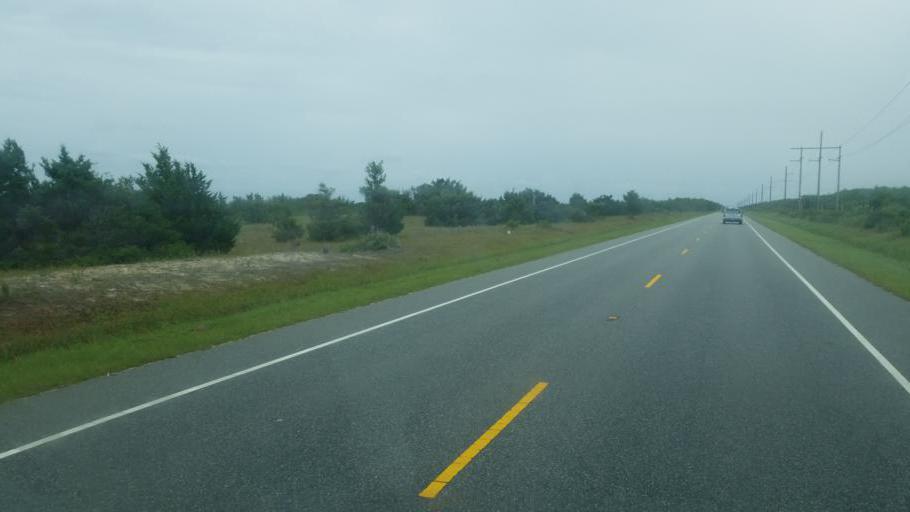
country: US
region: North Carolina
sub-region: Dare County
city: Buxton
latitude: 35.5222
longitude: -75.4753
